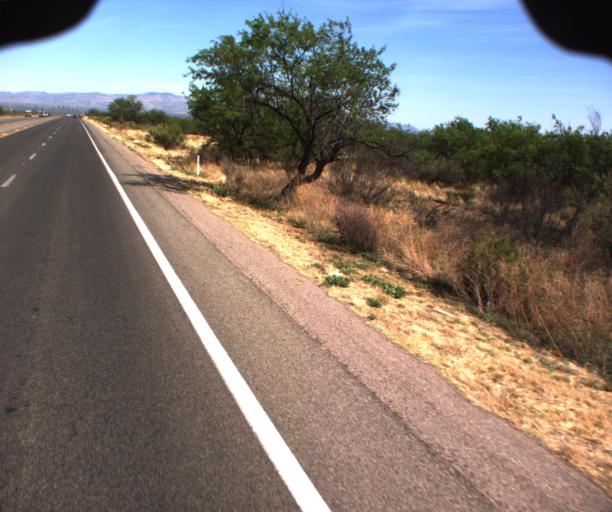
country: US
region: Arizona
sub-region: Cochise County
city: Sierra Vista Southeast
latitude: 31.5526
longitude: -110.1953
